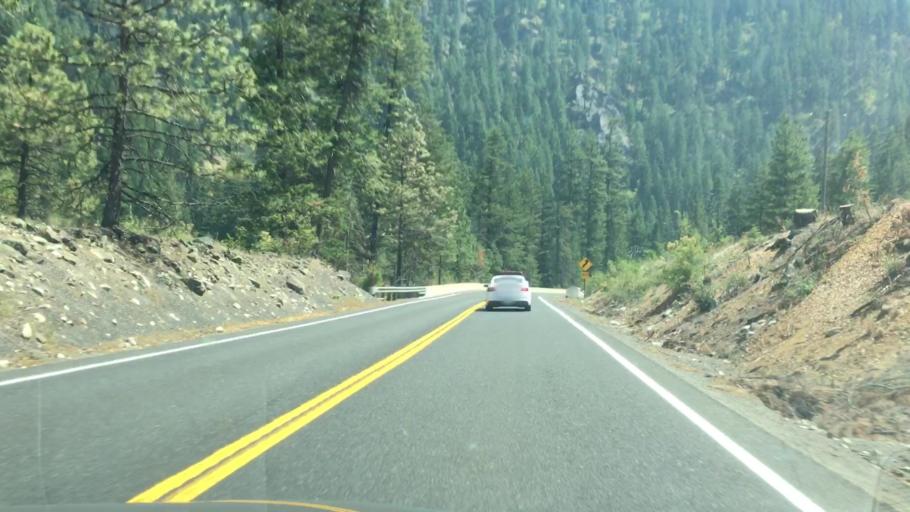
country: US
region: Idaho
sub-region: Valley County
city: McCall
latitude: 45.1476
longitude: -116.2901
